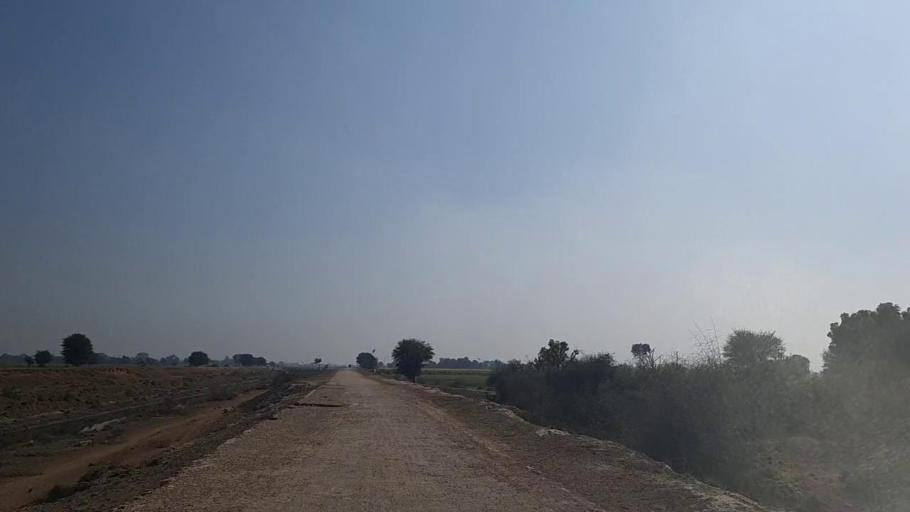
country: PK
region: Sindh
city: Shahpur Chakar
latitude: 26.1833
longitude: 68.5650
